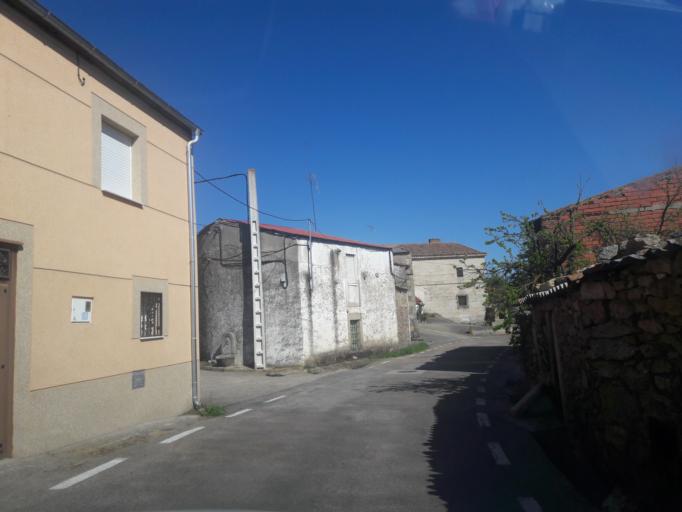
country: ES
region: Castille and Leon
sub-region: Provincia de Salamanca
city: Valsalabroso
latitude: 41.1542
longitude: -6.4879
